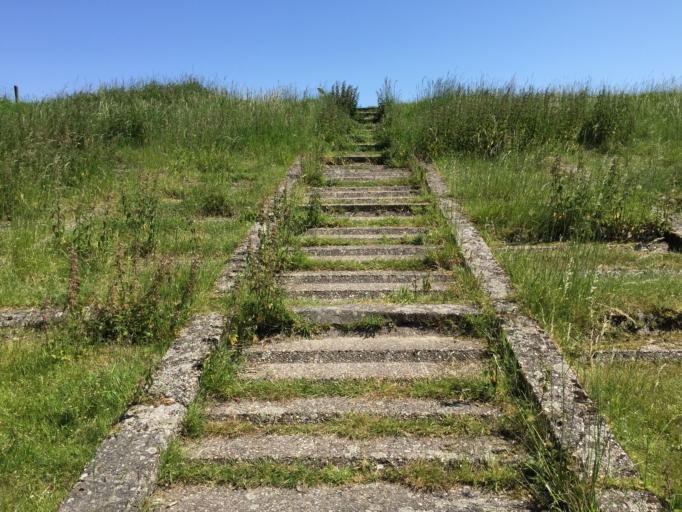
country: NL
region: Groningen
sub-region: Gemeente De Marne
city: Ulrum
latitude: 53.3403
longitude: 6.2991
